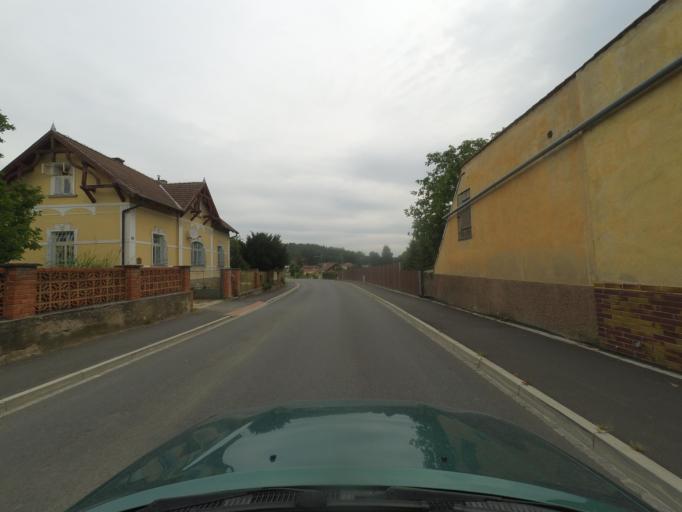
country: CZ
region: Plzensky
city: Horsovsky Tyn
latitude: 49.5329
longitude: 12.9497
